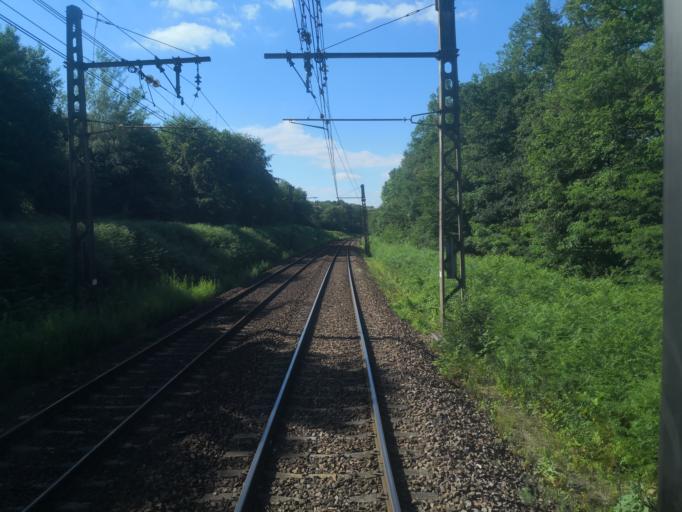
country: FR
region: Ile-de-France
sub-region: Departement de Seine-et-Marne
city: La Rochette
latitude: 48.4930
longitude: 2.6702
